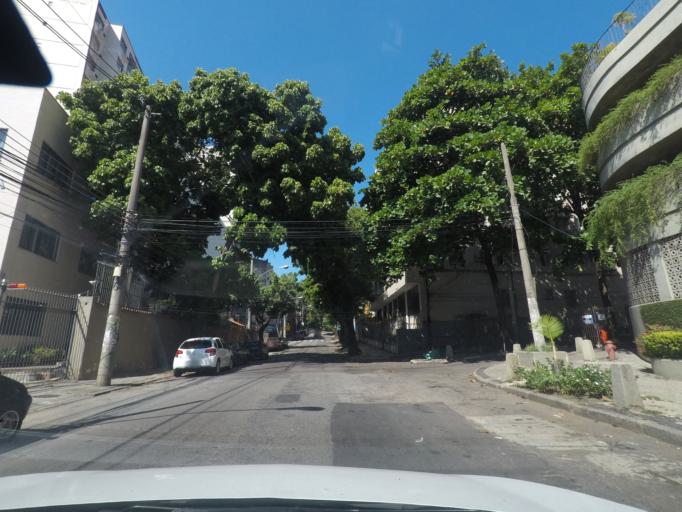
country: BR
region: Rio de Janeiro
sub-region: Rio De Janeiro
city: Rio de Janeiro
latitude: -22.9283
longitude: -43.2305
